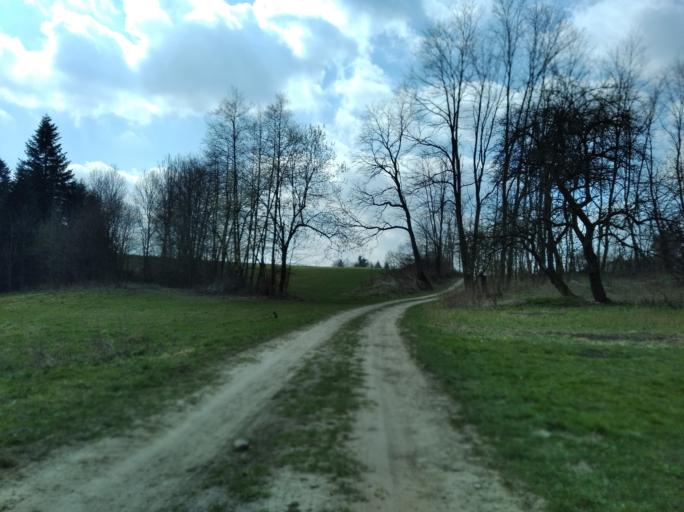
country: PL
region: Subcarpathian Voivodeship
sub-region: Powiat strzyzowski
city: Jawornik
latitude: 49.8242
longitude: 21.8575
